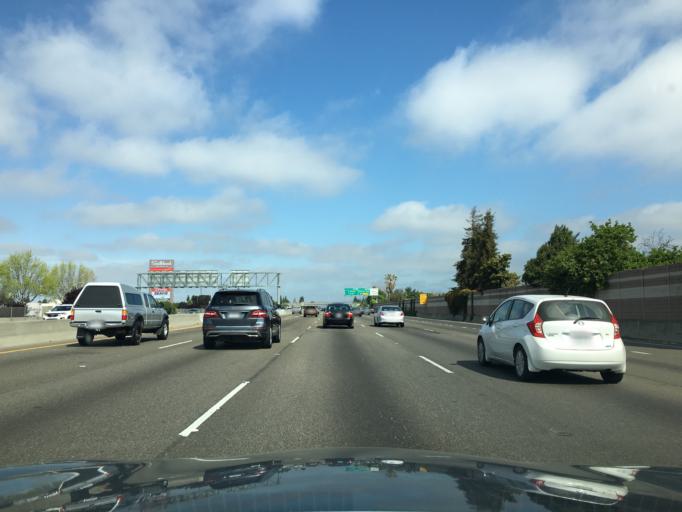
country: US
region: California
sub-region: Alameda County
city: Hayward
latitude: 37.6506
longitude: -122.0976
